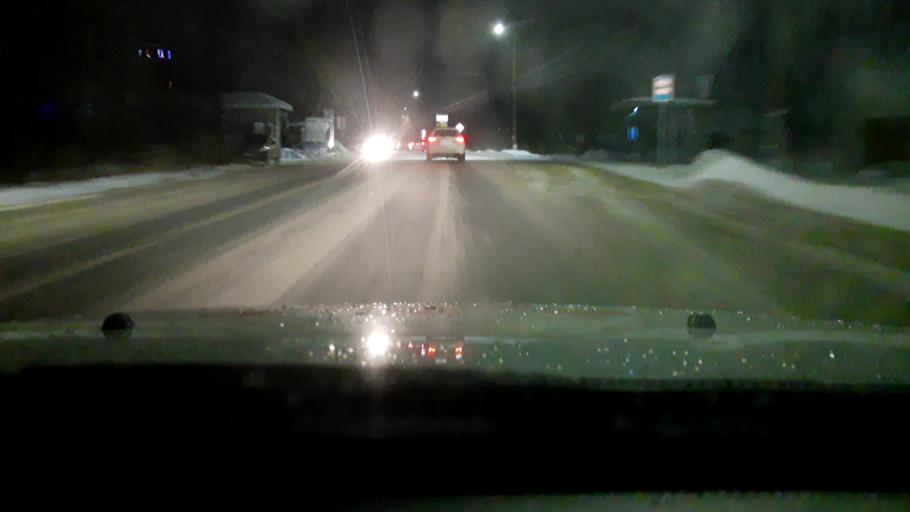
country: RU
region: Nizjnij Novgorod
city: Gorodets
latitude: 56.6618
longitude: 43.4695
